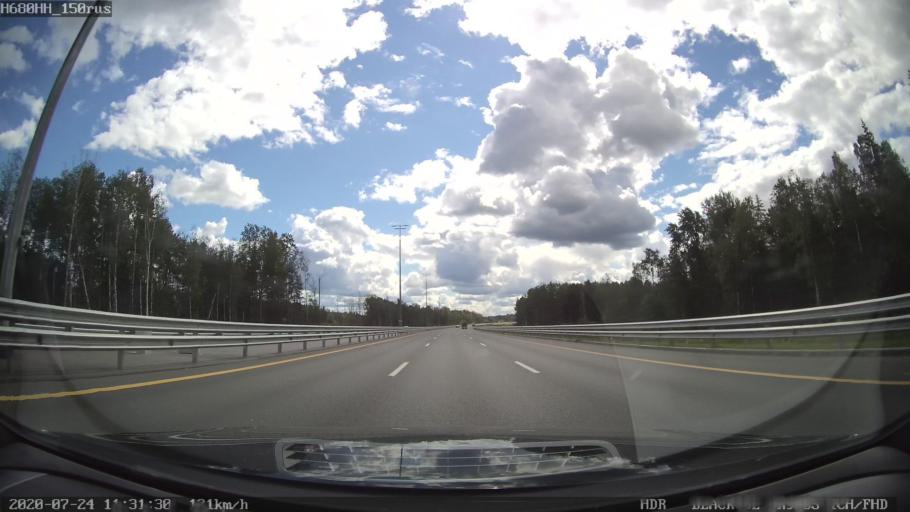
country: RU
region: Leningrad
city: Krasnyy Bor
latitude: 59.6554
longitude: 30.6395
